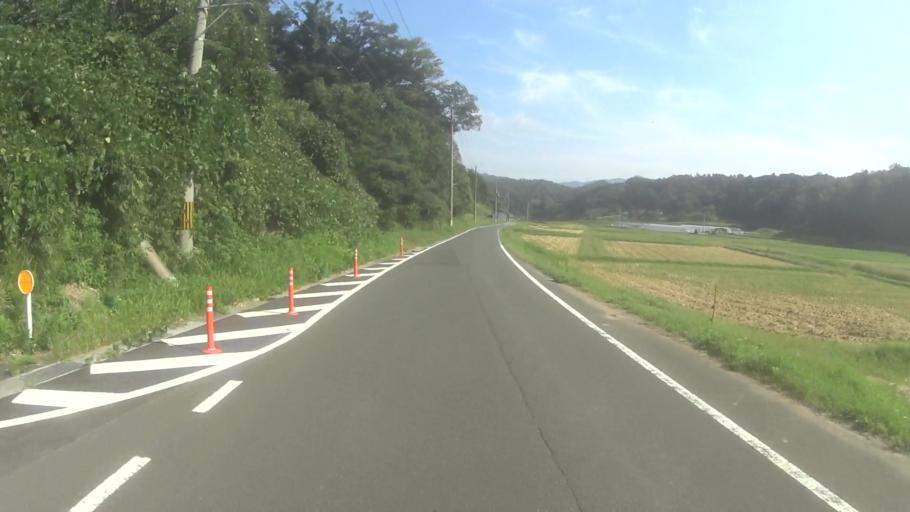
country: JP
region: Kyoto
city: Miyazu
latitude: 35.7101
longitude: 135.0841
